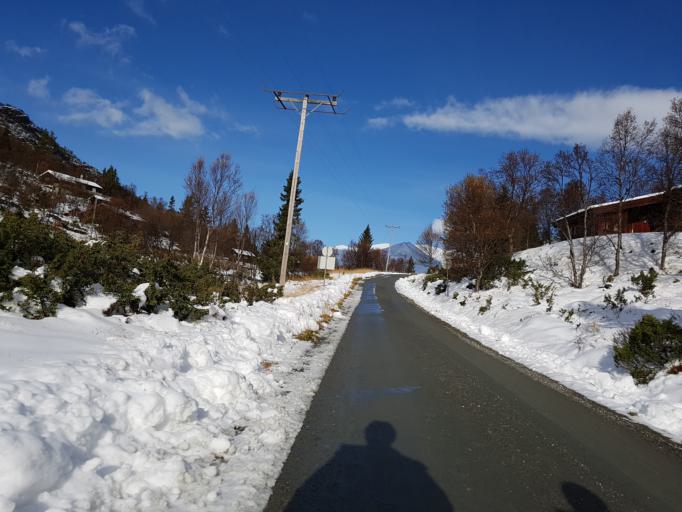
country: NO
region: Oppland
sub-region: Sel
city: Otta
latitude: 61.8182
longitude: 9.6775
